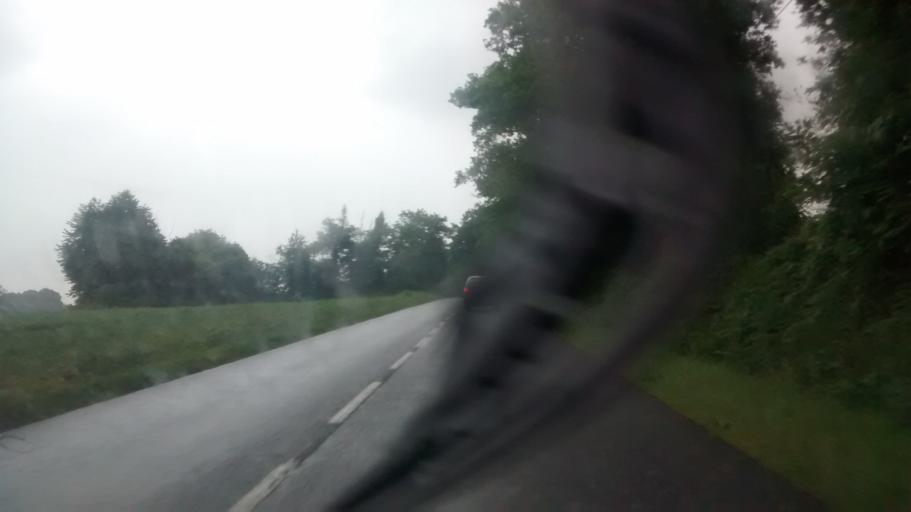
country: FR
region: Brittany
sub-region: Departement du Morbihan
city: La Gacilly
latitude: 47.7819
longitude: -2.1845
